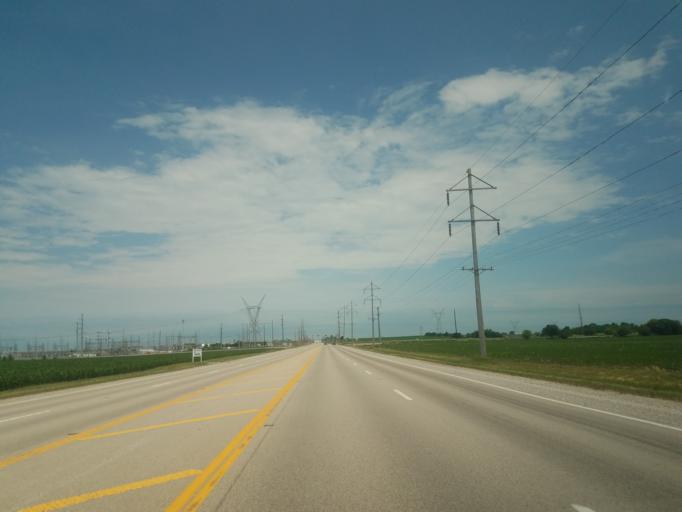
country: US
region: Illinois
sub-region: McLean County
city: Downs
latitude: 40.4480
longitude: -88.9017
